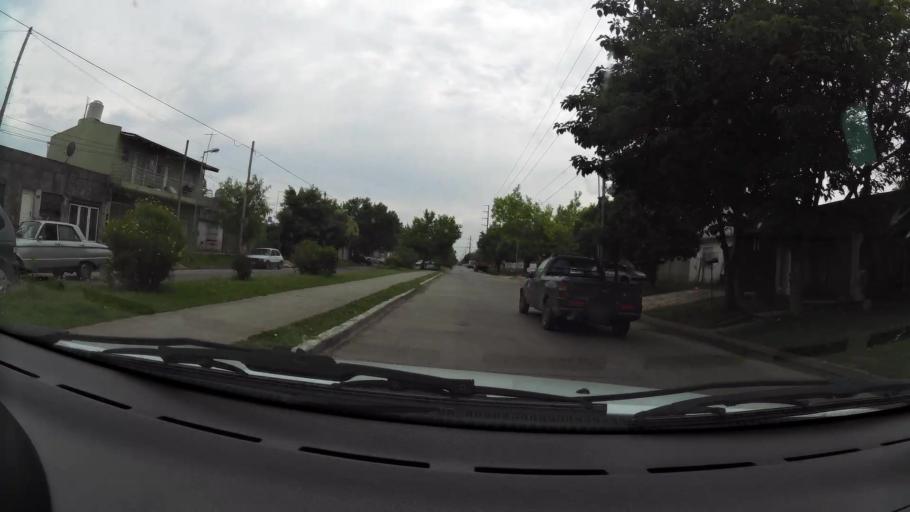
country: AR
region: Buenos Aires
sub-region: Partido de La Plata
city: La Plata
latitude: -34.9169
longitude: -57.9992
